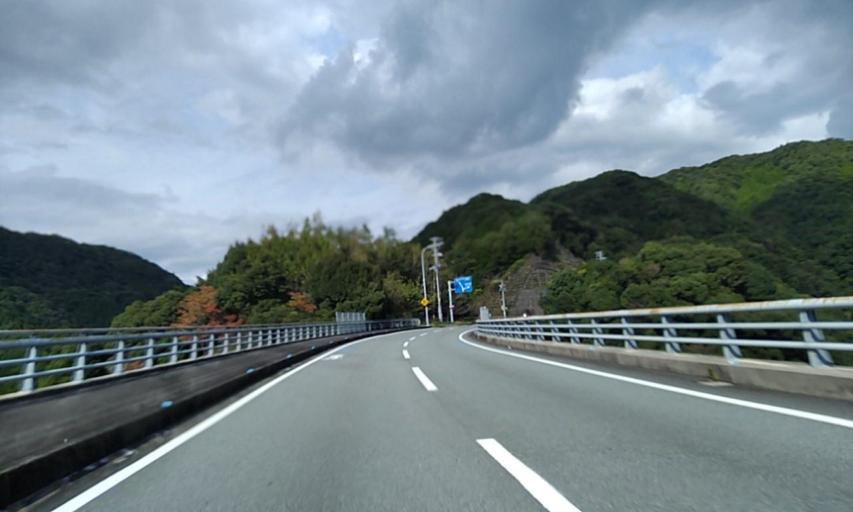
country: JP
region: Mie
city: Owase
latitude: 34.2489
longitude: 136.4033
